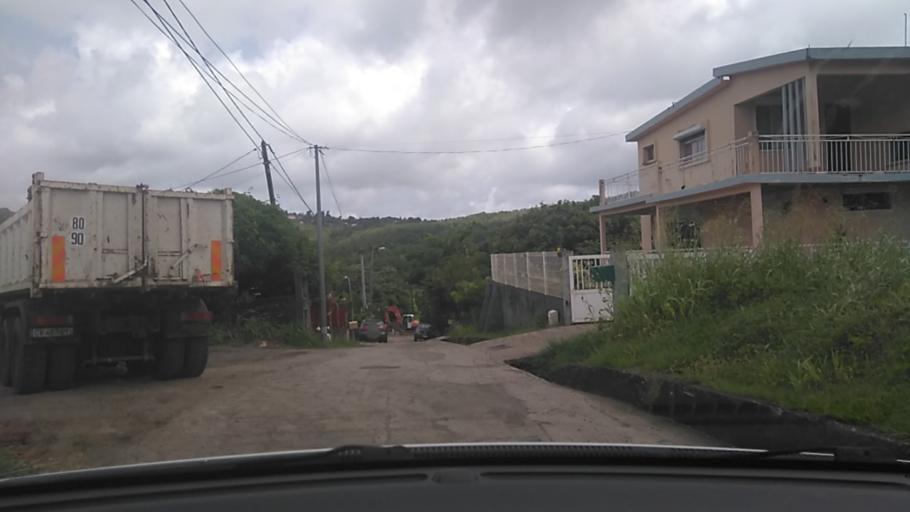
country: MQ
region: Martinique
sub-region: Martinique
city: Saint-Esprit
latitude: 14.5614
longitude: -60.9319
